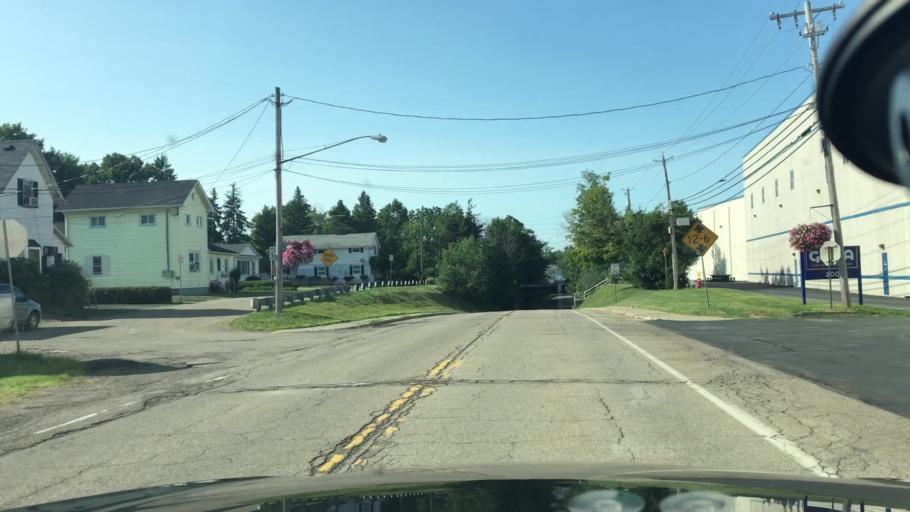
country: US
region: New York
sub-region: Erie County
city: Angola
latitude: 42.6298
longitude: -79.0274
